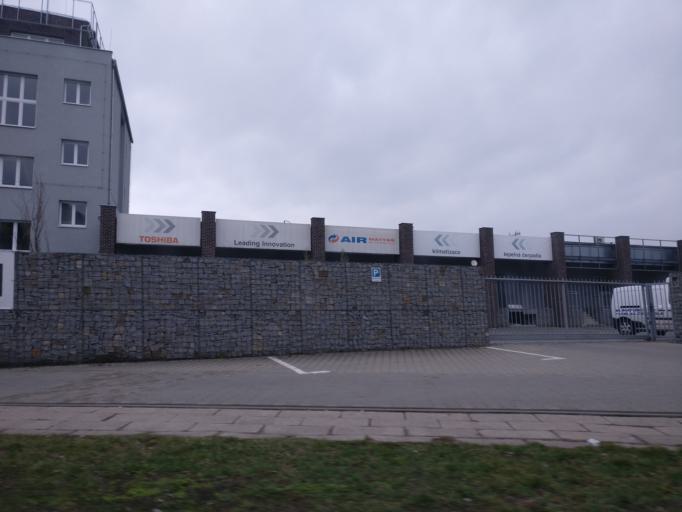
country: CZ
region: Pardubicky
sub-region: Okres Pardubice
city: Pardubice
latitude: 50.0326
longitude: 15.7621
